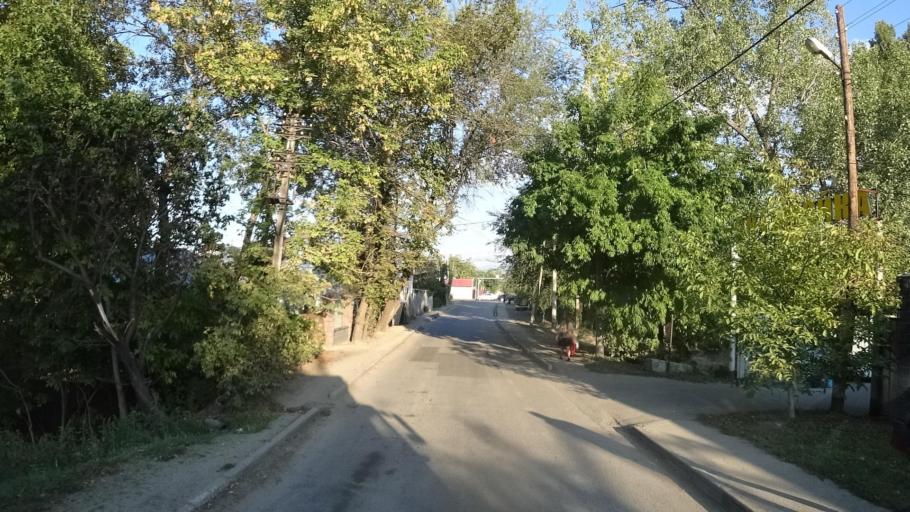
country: KZ
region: Almaty Qalasy
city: Almaty
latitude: 43.3074
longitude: 76.9656
